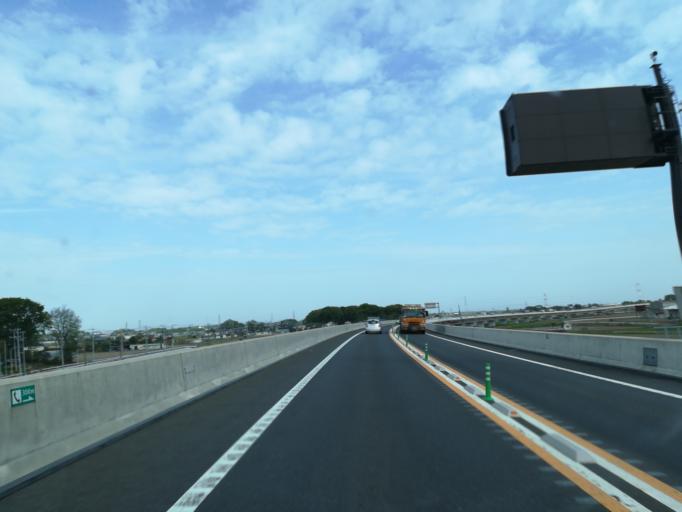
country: JP
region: Ibaraki
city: Sakai
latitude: 36.1010
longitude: 139.7582
